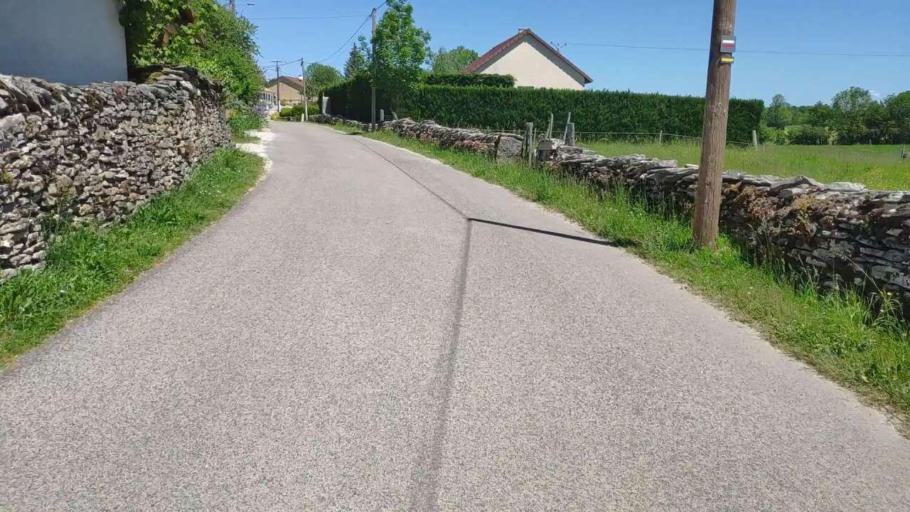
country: FR
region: Franche-Comte
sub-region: Departement du Jura
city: Perrigny
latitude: 46.7168
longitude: 5.6449
